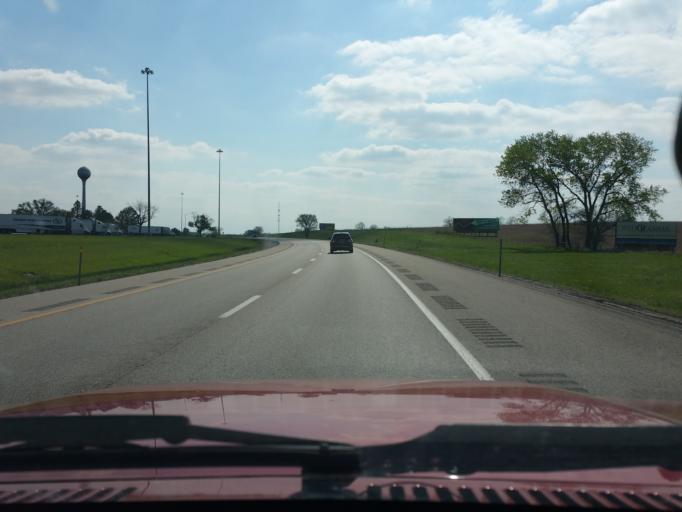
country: US
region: Kansas
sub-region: Douglas County
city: Eudora
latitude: 39.0216
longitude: -95.1343
